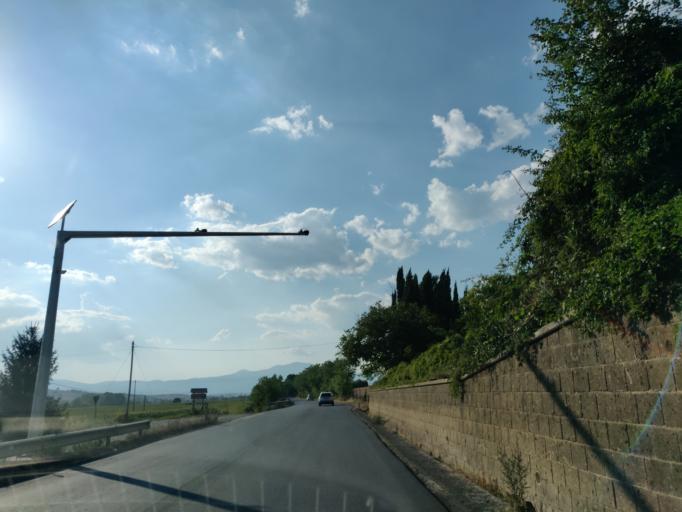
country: IT
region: Latium
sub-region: Provincia di Viterbo
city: Proceno
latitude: 42.7802
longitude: 11.8361
